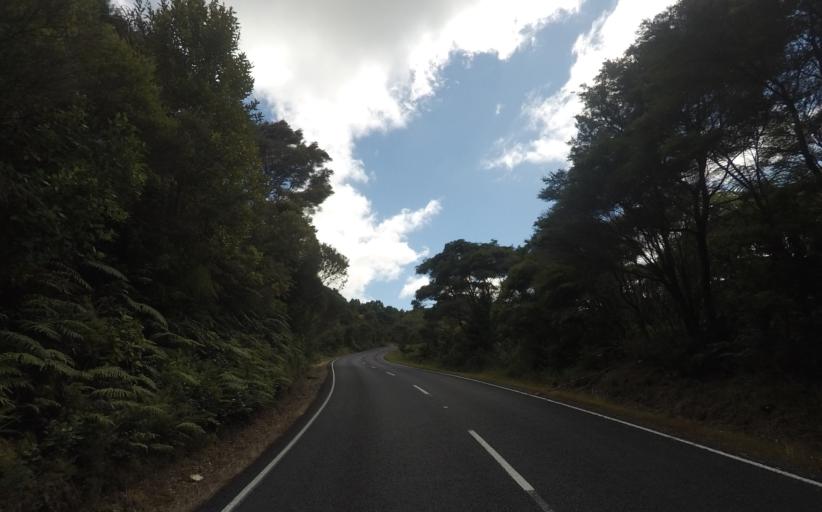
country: NZ
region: Auckland
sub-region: Auckland
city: Muriwai Beach
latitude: -36.8629
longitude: 174.5156
